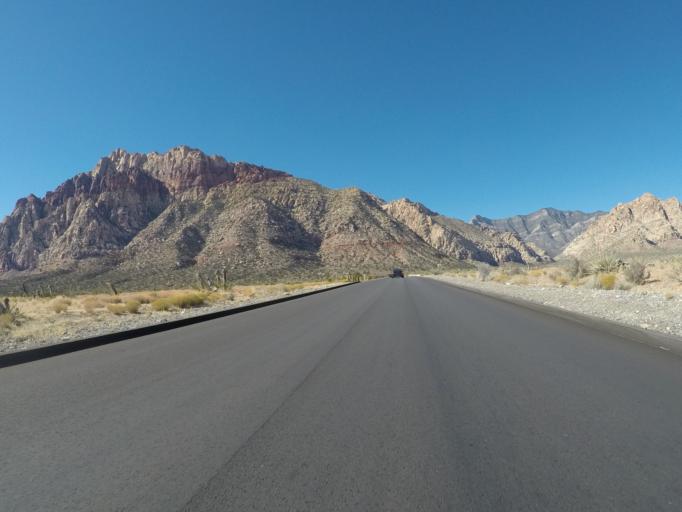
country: US
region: Nevada
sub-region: Clark County
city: Summerlin South
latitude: 36.1386
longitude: -115.4700
